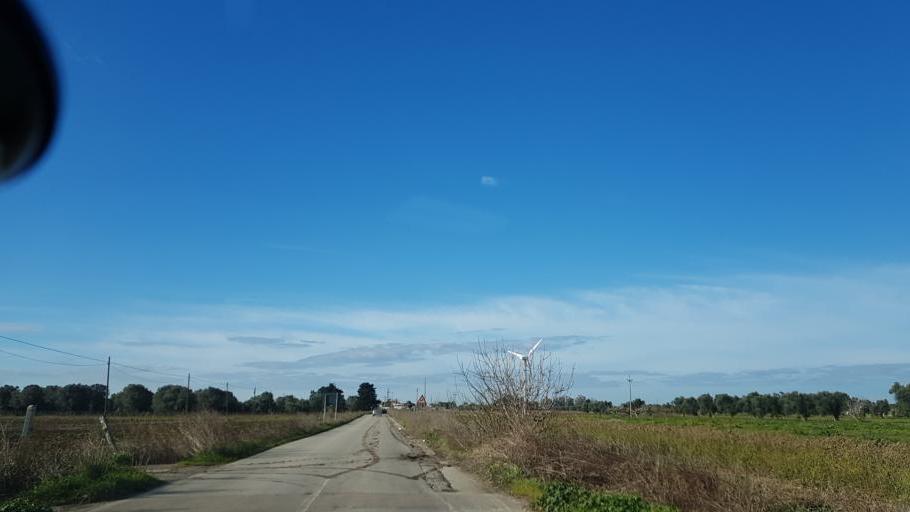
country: IT
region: Apulia
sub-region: Provincia di Brindisi
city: Tuturano
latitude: 40.5531
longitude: 17.9919
